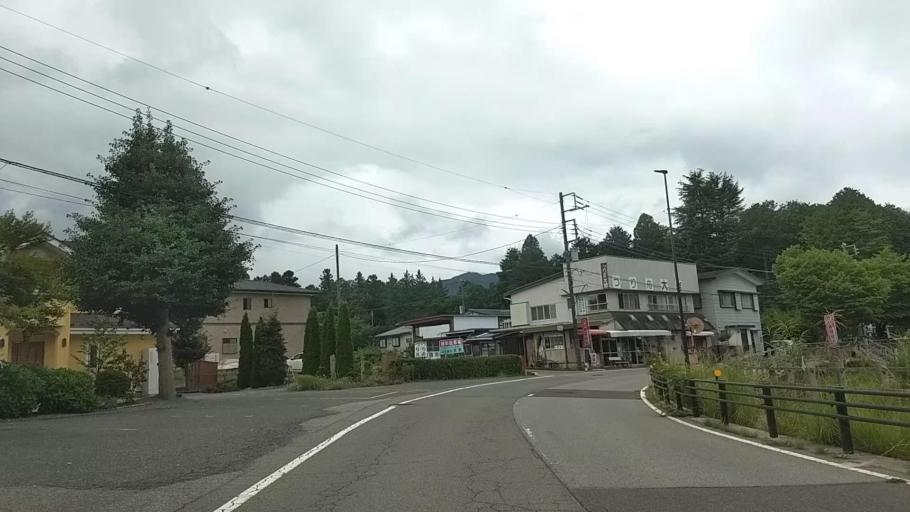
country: JP
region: Yamanashi
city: Fujikawaguchiko
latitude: 35.5110
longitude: 138.7479
